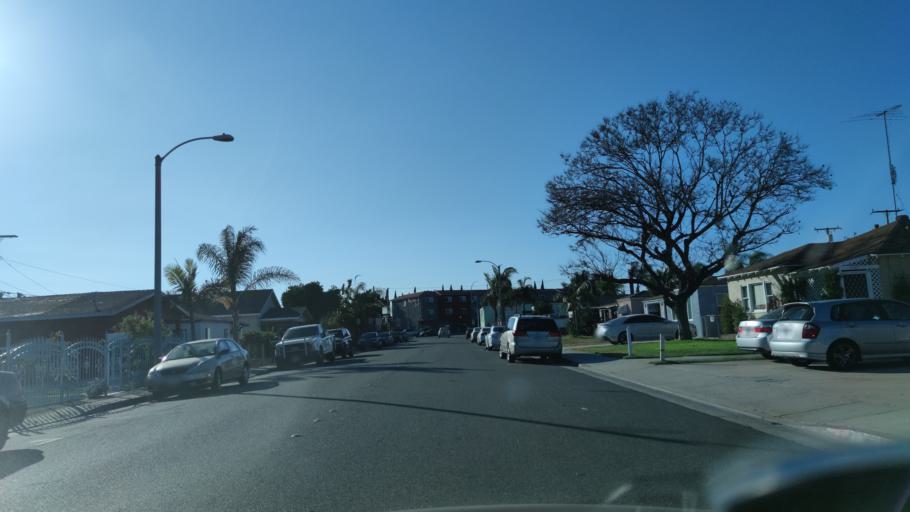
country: US
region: California
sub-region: Los Angeles County
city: Maywood
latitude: 33.9904
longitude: -118.1838
